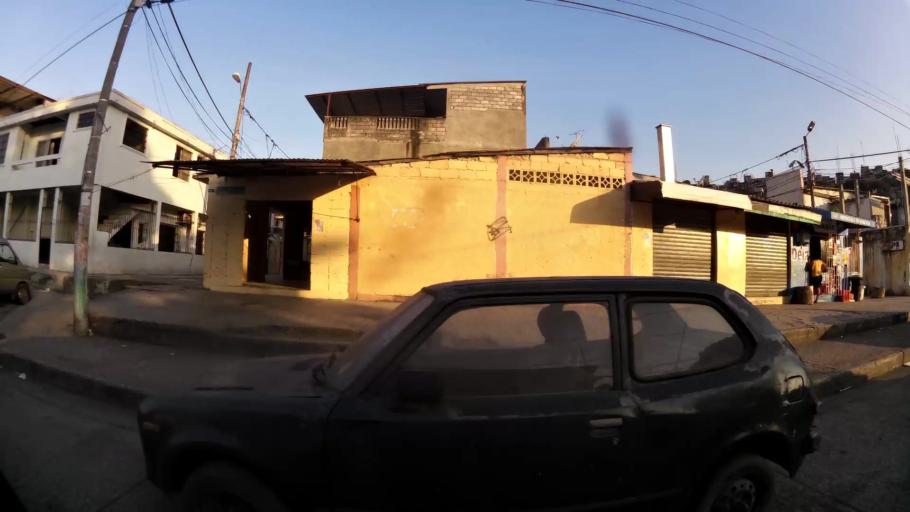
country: EC
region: Guayas
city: Guayaquil
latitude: -2.1481
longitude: -79.9212
